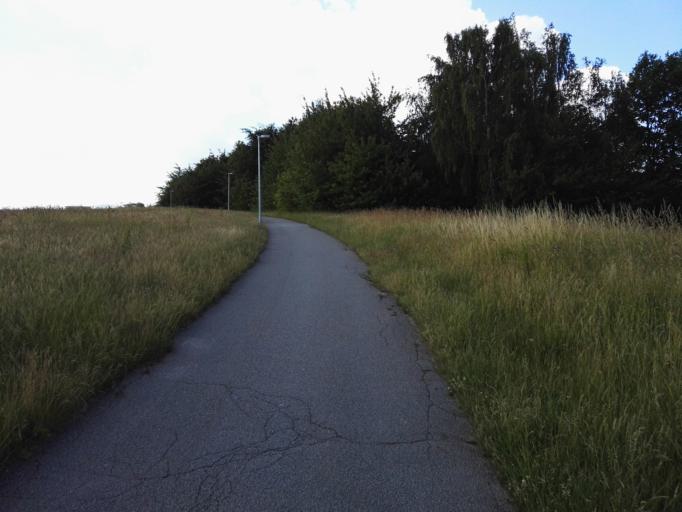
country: DK
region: Capital Region
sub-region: Ballerup Kommune
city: Ballerup
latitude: 55.7367
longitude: 12.3956
